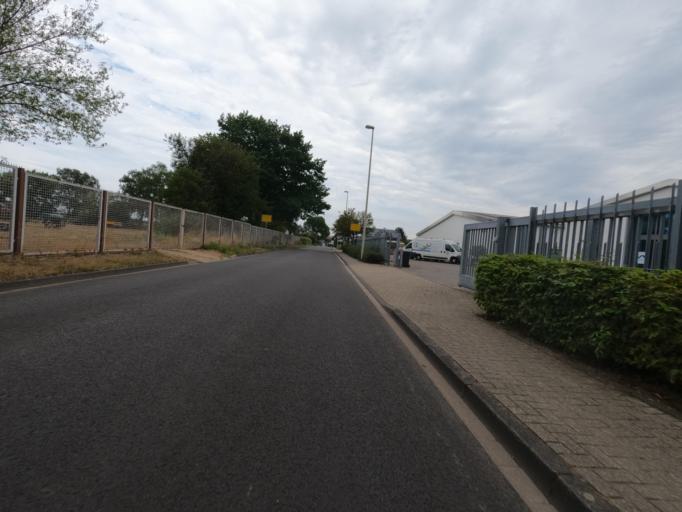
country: DE
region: North Rhine-Westphalia
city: Geilenkirchen
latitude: 50.9852
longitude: 6.1156
